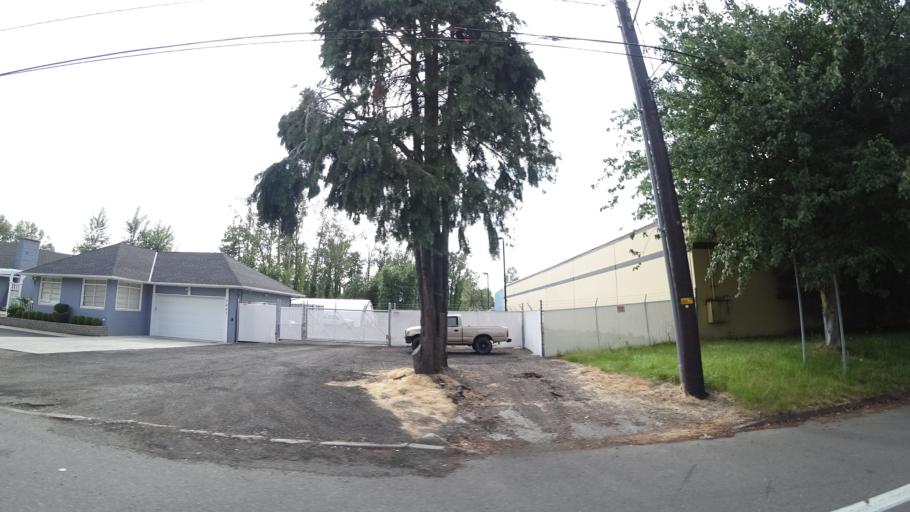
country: US
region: Washington
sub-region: Clark County
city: Vancouver
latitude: 45.5773
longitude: -122.6334
